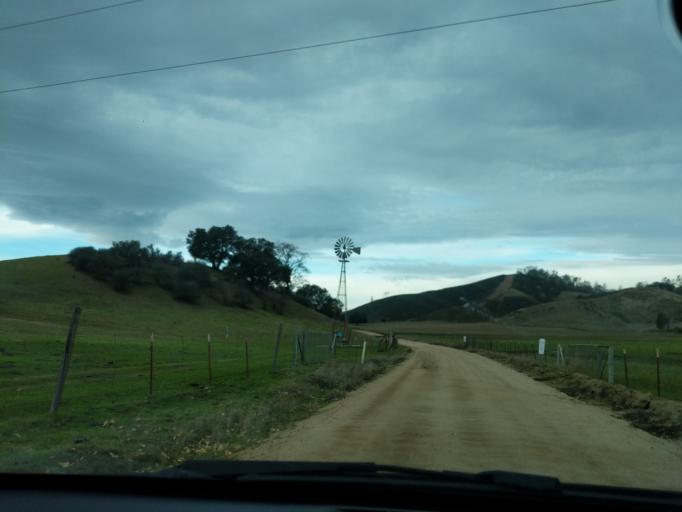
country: US
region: California
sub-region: Monterey County
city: Soledad
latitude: 36.5391
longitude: -121.2927
